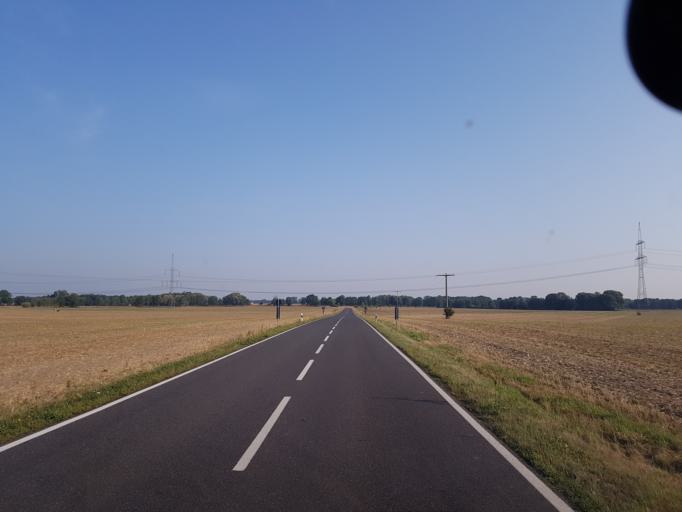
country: DE
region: Brandenburg
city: Finsterwalde
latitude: 51.6482
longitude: 13.7349
